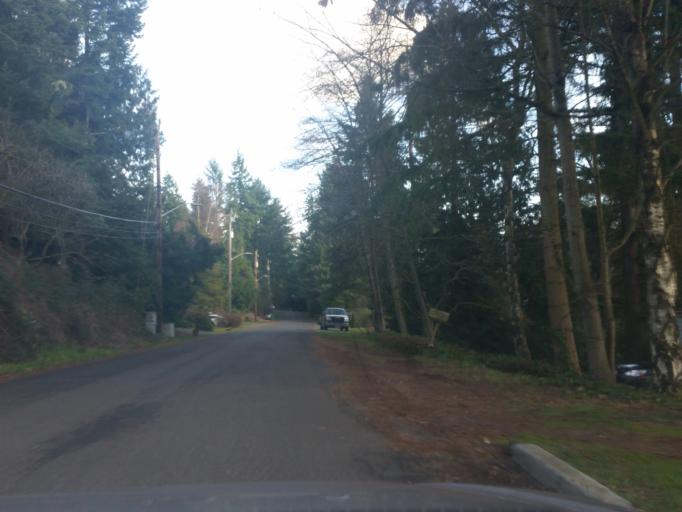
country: US
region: Washington
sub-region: King County
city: Shoreline
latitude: 47.7064
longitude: -122.3124
